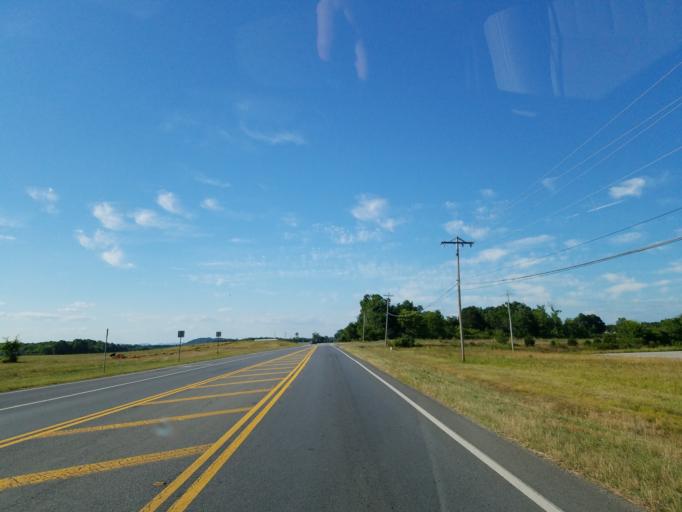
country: US
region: Georgia
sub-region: Gordon County
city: Calhoun
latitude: 34.4448
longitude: -84.9357
